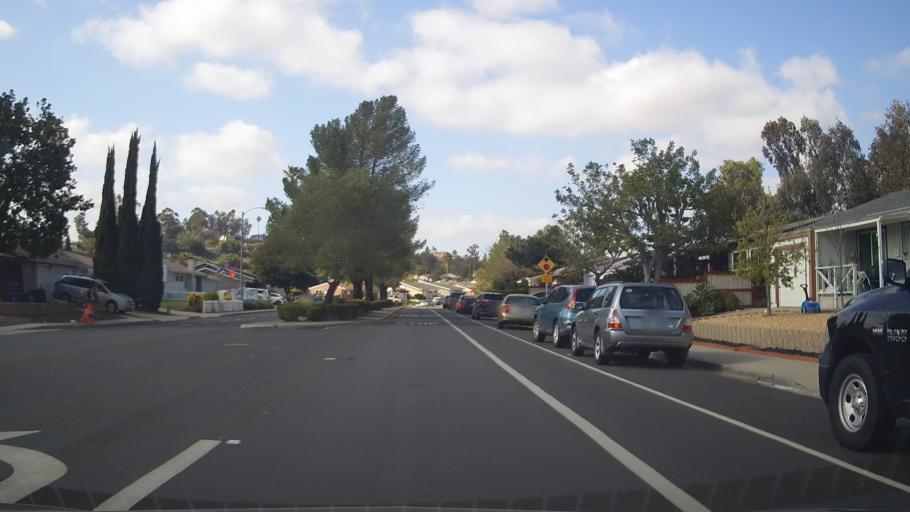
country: US
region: California
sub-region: San Diego County
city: Poway
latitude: 32.9576
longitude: -117.0541
